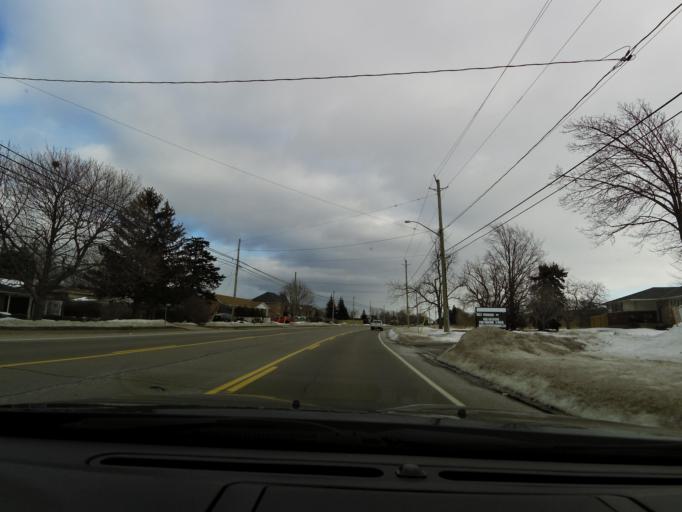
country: CA
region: Ontario
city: Hamilton
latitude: 43.2060
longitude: -79.6251
